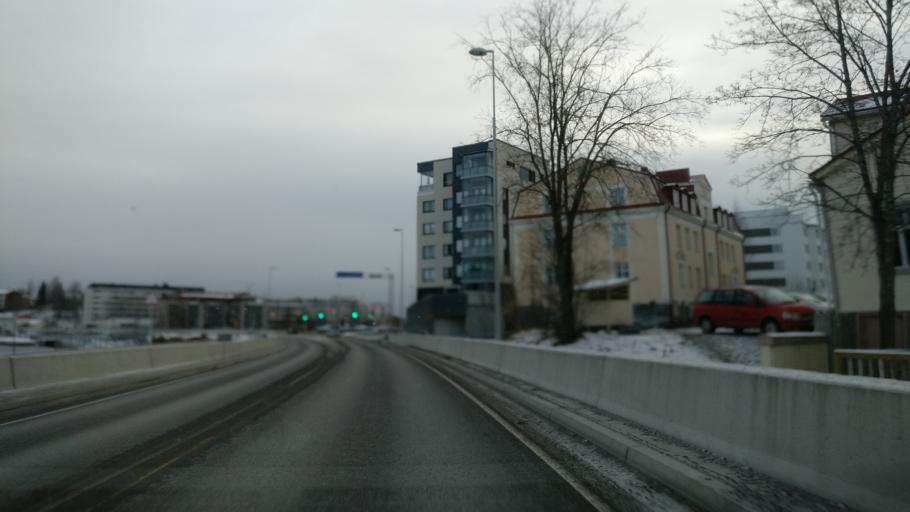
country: FI
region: Southern Savonia
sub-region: Savonlinna
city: Savonlinna
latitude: 61.8713
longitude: 28.8821
